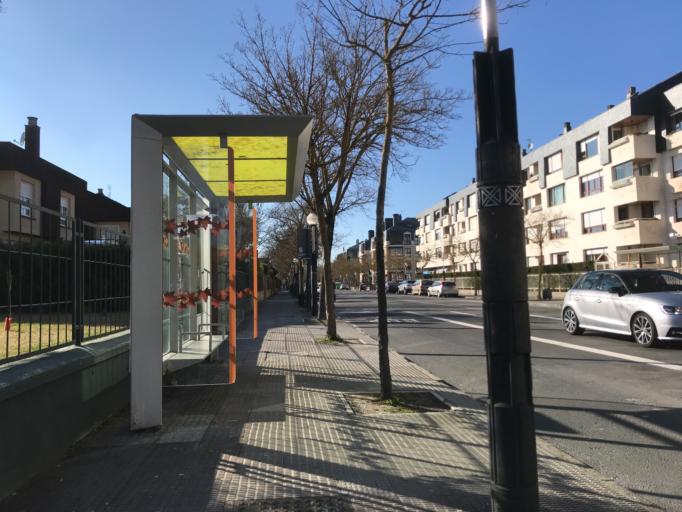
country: ES
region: Basque Country
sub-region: Provincia de Alava
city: Gasteiz / Vitoria
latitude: 42.8375
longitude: -2.6804
